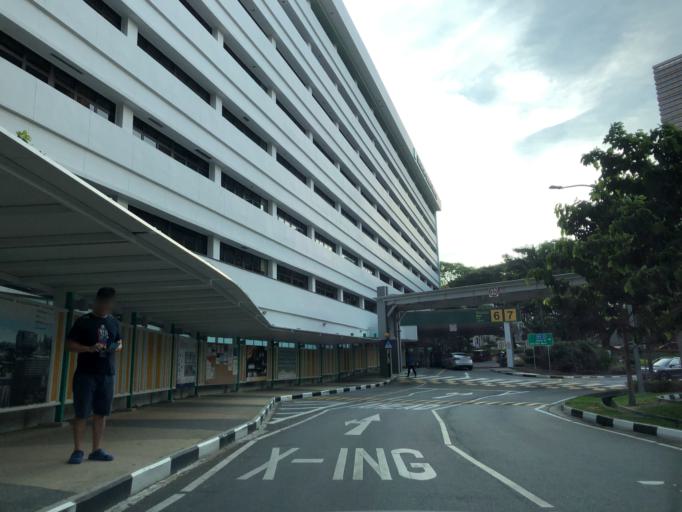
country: SG
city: Singapore
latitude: 1.2809
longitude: 103.8356
